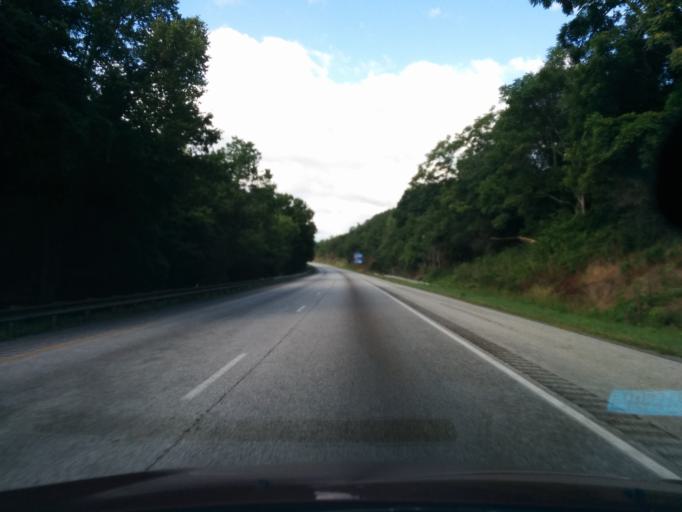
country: US
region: Virginia
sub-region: Rockbridge County
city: Glasgow
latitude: 37.6936
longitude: -79.4790
